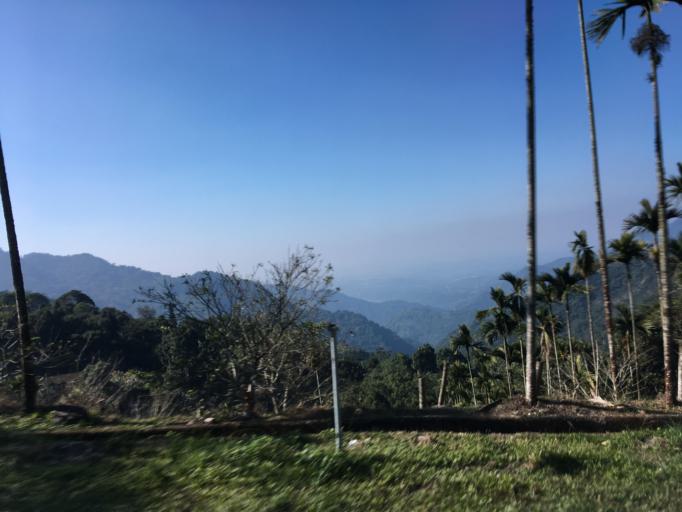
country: TW
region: Taiwan
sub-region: Chiayi
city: Jiayi Shi
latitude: 23.4063
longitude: 120.6488
